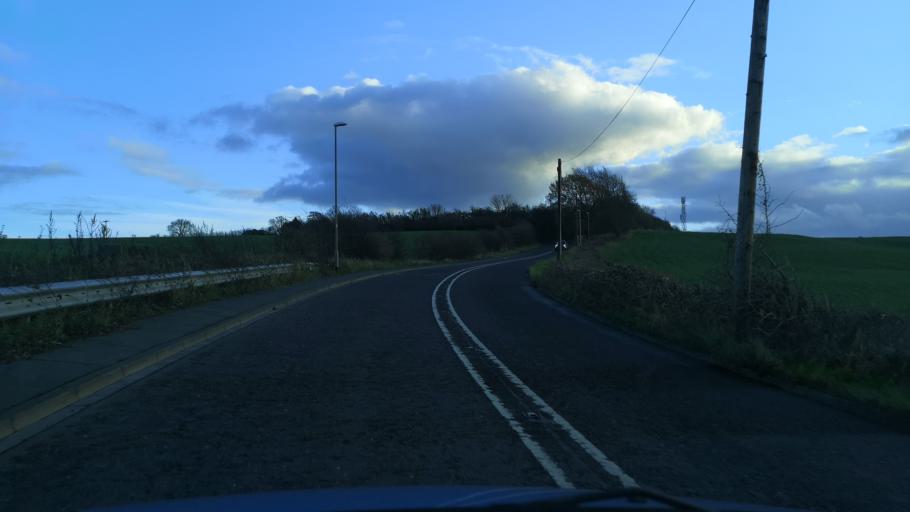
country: GB
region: England
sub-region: City and Borough of Wakefield
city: Ossett
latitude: 53.7084
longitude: -1.5612
